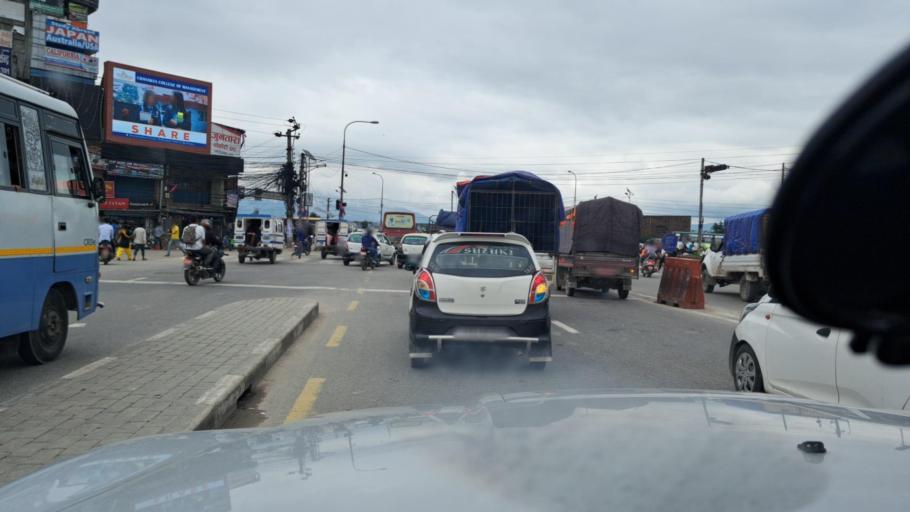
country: NP
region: Central Region
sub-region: Bagmati Zone
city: Patan
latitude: 27.6785
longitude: 85.3489
